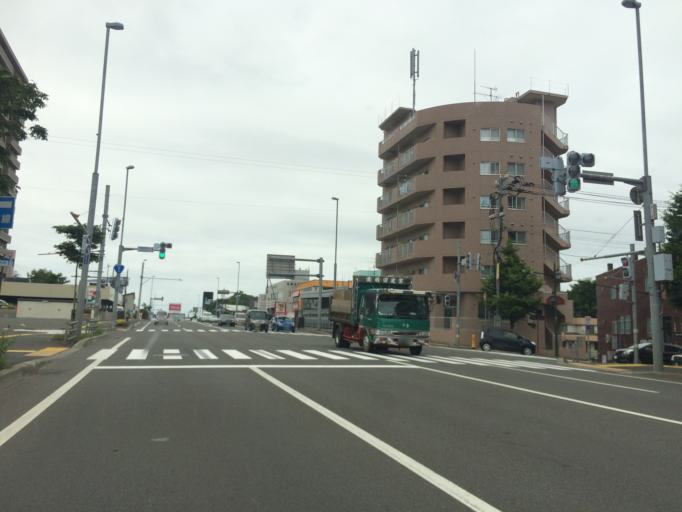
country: JP
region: Hokkaido
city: Sapporo
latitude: 43.1185
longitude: 141.2395
